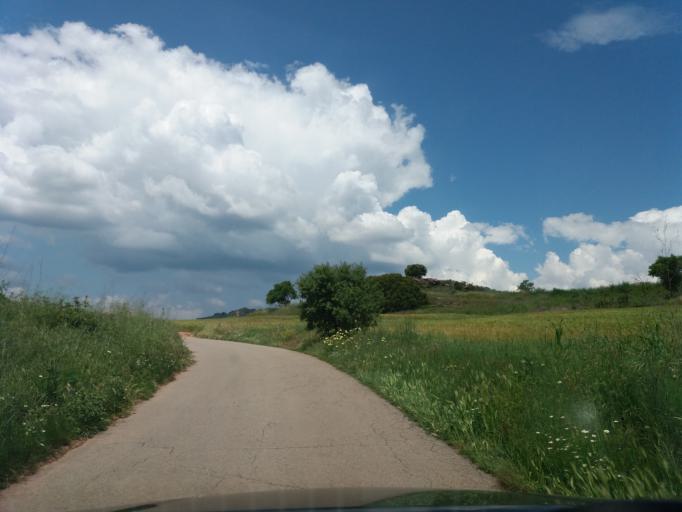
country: ES
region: Catalonia
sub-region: Provincia de Barcelona
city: Sant Joan de Vilatorrada
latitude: 41.7444
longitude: 1.7936
